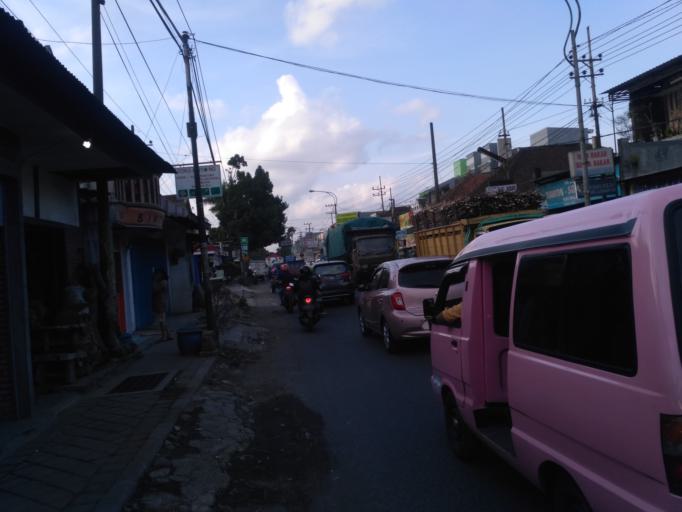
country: ID
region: East Java
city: Kebonsari
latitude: -8.0247
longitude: 112.6171
